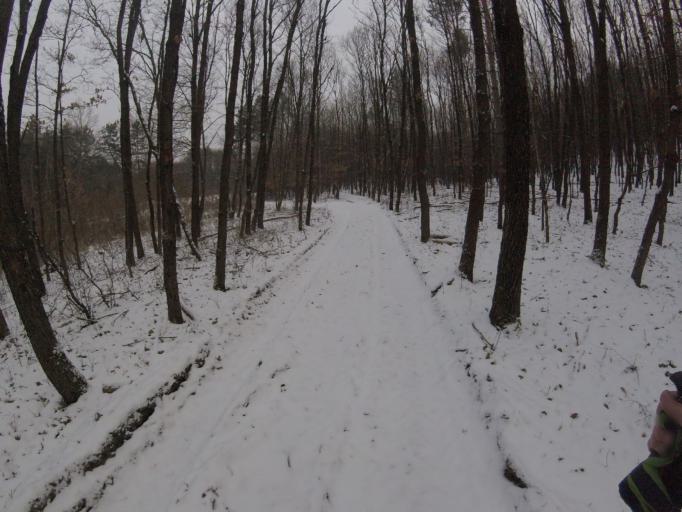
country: HU
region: Heves
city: Sirok
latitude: 47.9785
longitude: 20.1933
